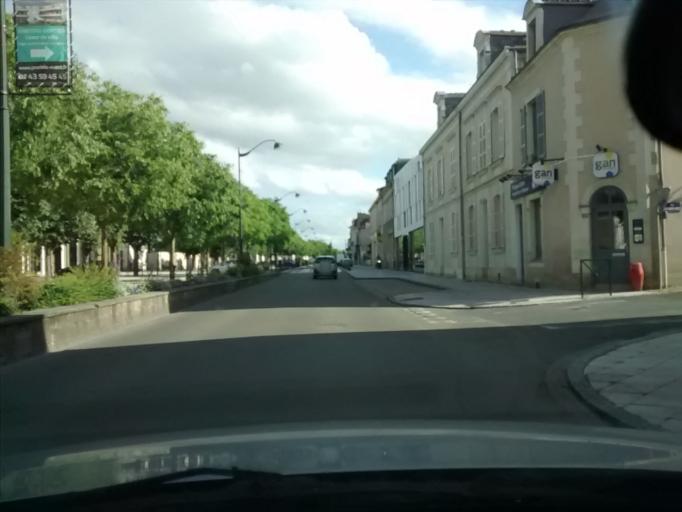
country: FR
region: Pays de la Loire
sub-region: Departement de la Mayenne
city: Chateau-Gontier
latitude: 47.8287
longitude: -0.7083
